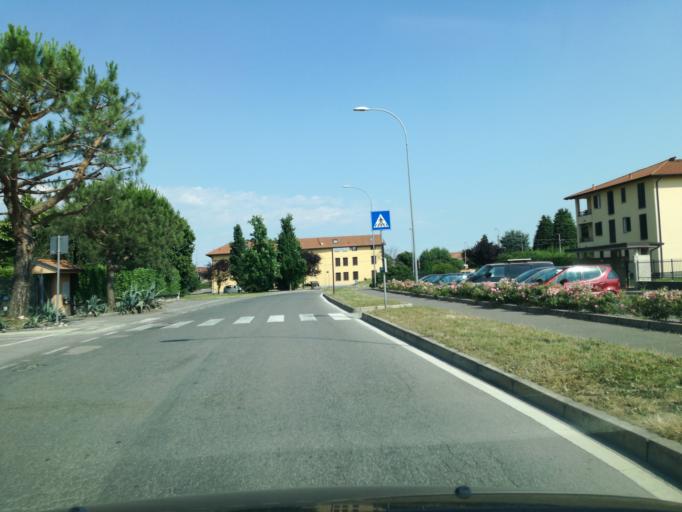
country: IT
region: Lombardy
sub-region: Provincia di Lecco
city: Merate
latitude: 45.6828
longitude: 9.4101
